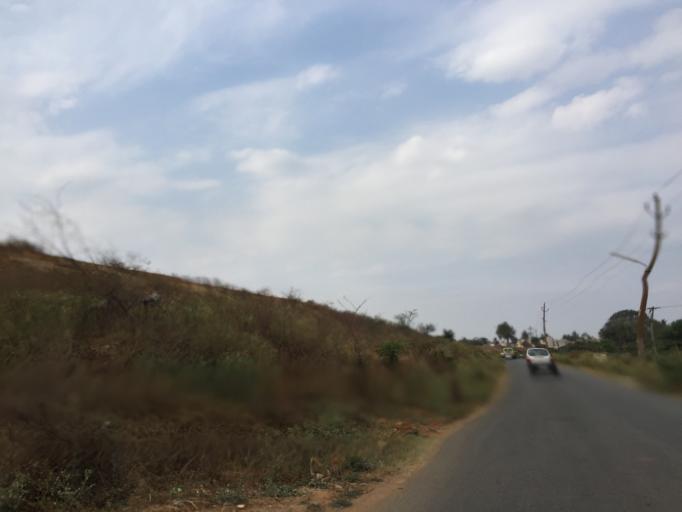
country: IN
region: Karnataka
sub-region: Chikkaballapur
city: Chik Ballapur
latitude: 13.4240
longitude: 77.7211
